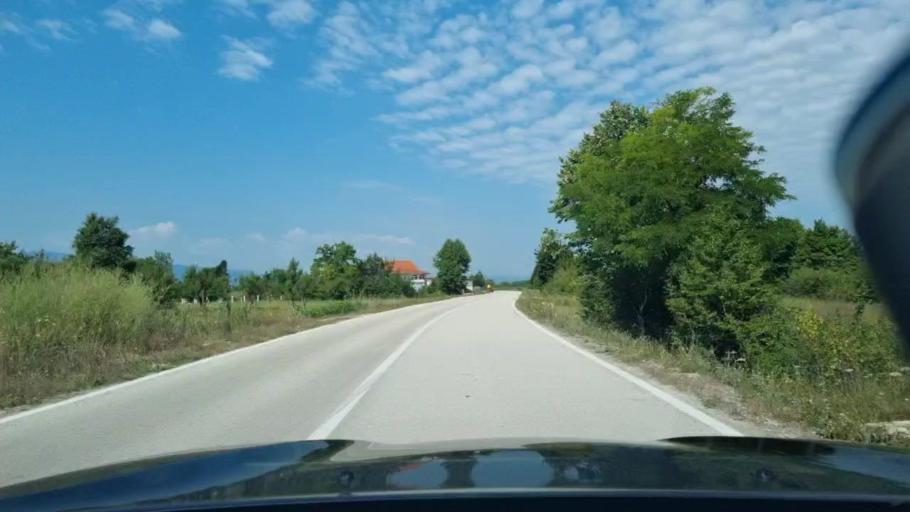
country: BA
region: Federation of Bosnia and Herzegovina
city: Ostrozac
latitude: 44.8894
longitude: 15.9458
